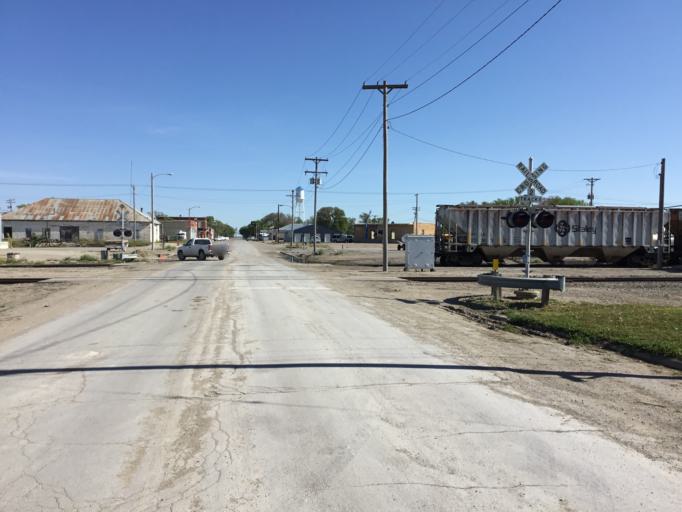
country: US
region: Kansas
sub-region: Smith County
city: Smith Center
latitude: 39.7633
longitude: -99.0319
